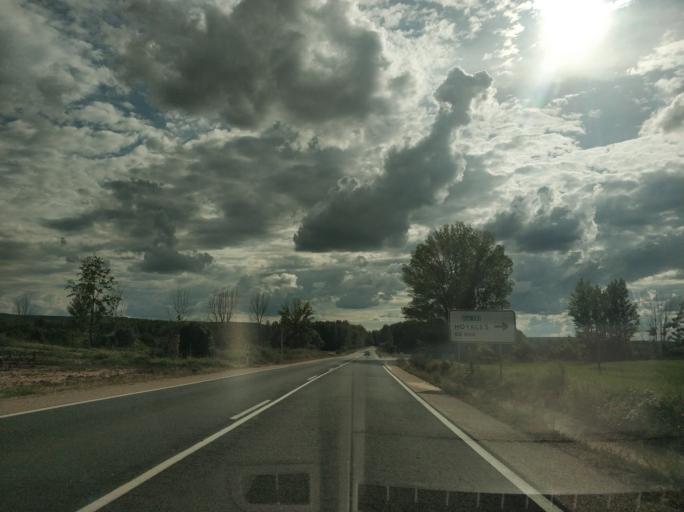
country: ES
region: Castille and Leon
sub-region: Provincia de Burgos
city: Haza
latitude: 41.6331
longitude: -3.8376
